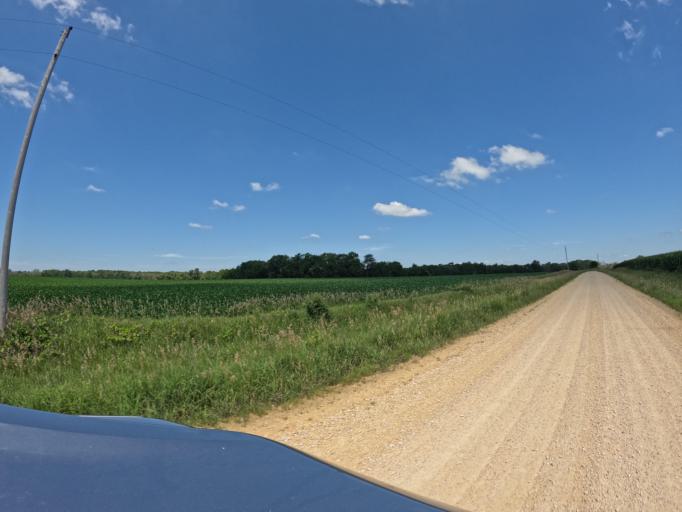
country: US
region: Iowa
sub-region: Clinton County
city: De Witt
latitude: 41.7706
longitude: -90.4324
